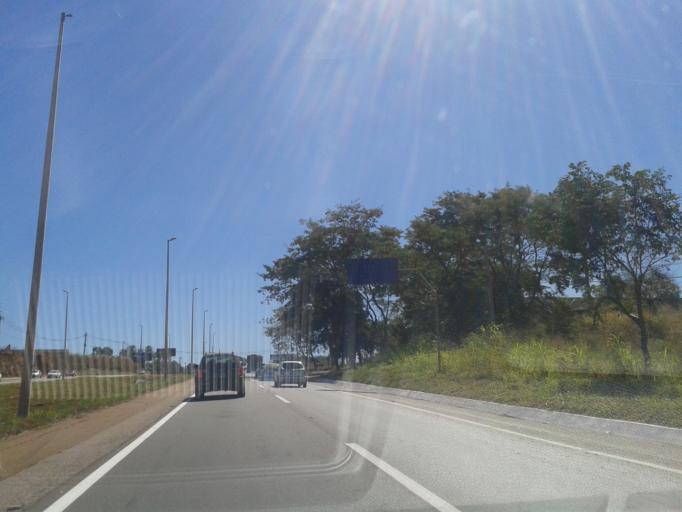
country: BR
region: Goias
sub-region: Goiania
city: Goiania
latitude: -16.6418
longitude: -49.3407
